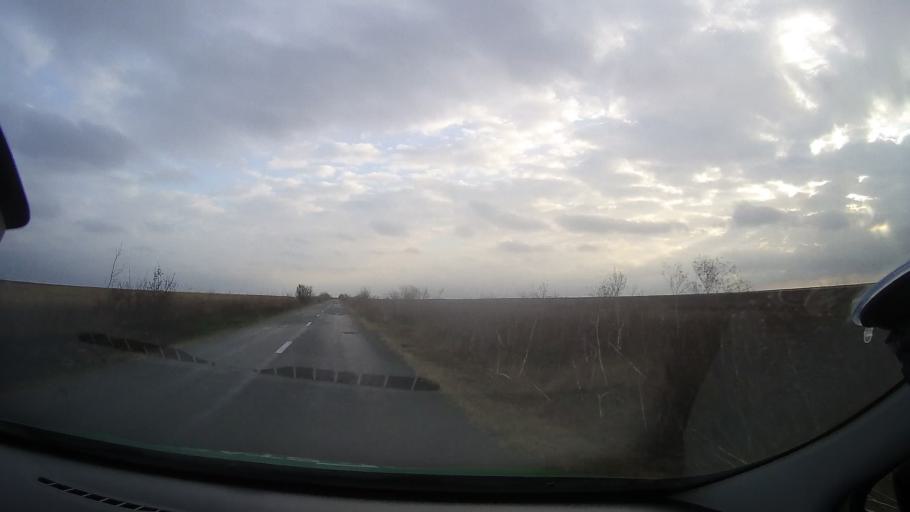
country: RO
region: Constanta
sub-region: Comuna Pestera
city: Pestera
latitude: 44.1389
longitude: 28.1177
